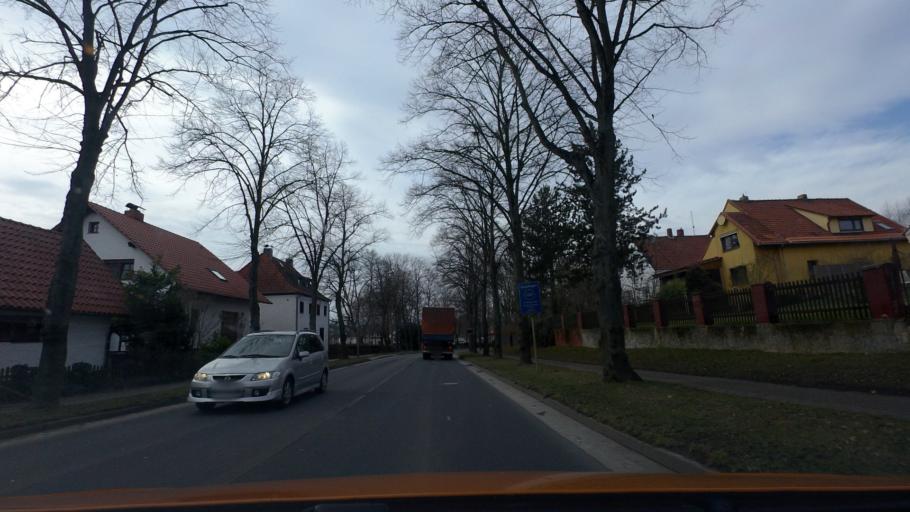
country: DE
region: Lower Saxony
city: Supplingen
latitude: 52.2264
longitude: 10.9134
